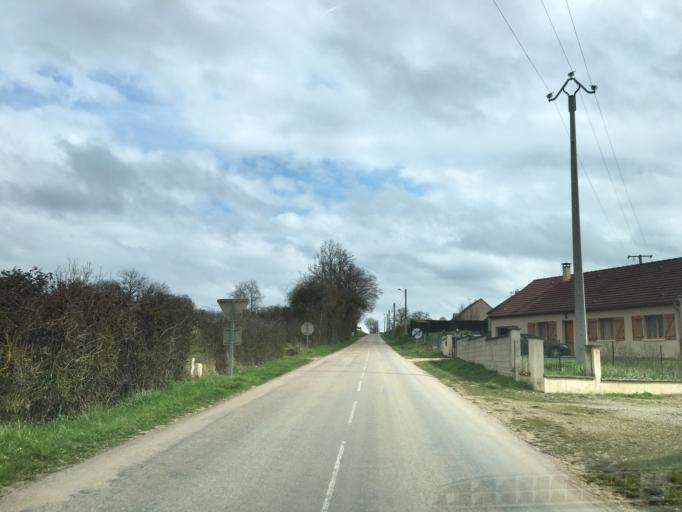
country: FR
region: Bourgogne
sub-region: Departement de l'Yonne
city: Pourrain
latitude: 47.7946
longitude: 3.3847
